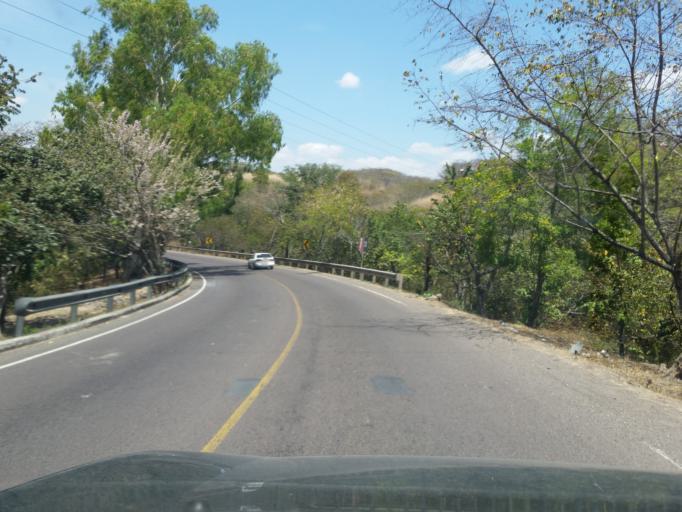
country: NI
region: Esteli
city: Esteli
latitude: 13.0335
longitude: -86.3192
